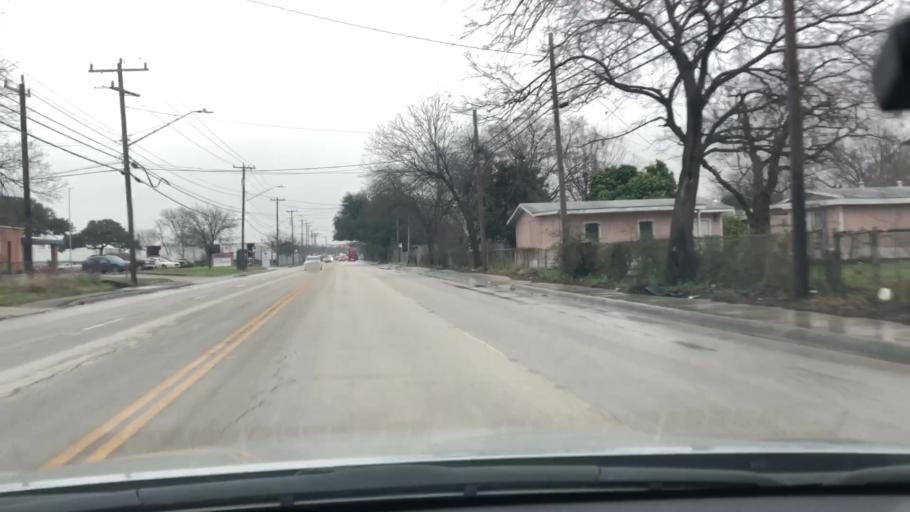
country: US
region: Texas
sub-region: Bexar County
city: Kirby
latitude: 29.4356
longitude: -98.4096
